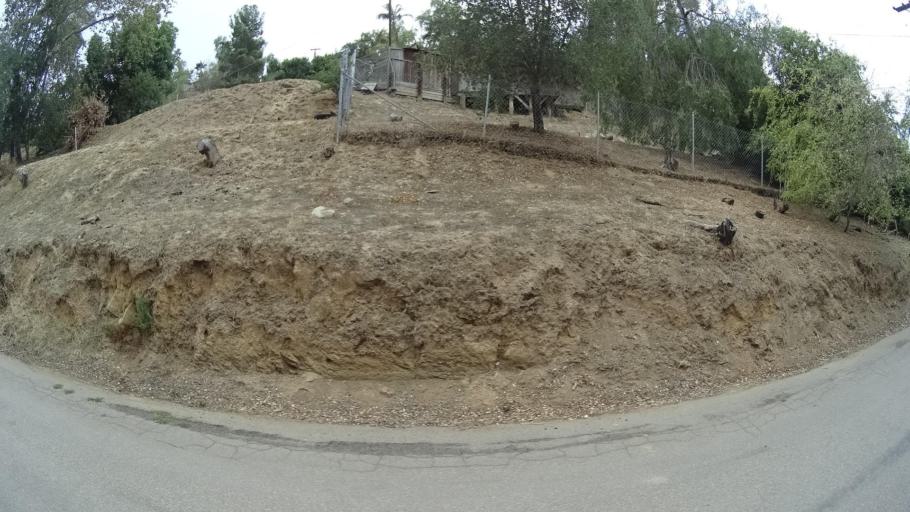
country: US
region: California
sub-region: San Diego County
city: Escondido
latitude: 33.1380
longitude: -117.1125
